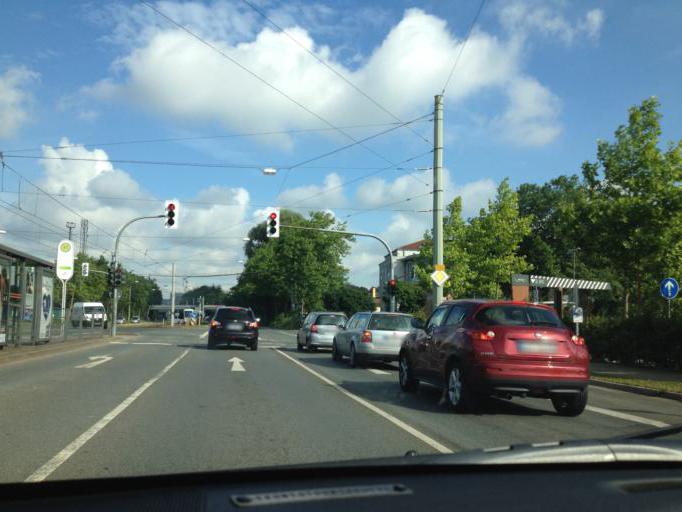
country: DE
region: North Rhine-Westphalia
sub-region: Regierungsbezirk Arnsberg
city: Bochum
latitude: 51.4682
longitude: 7.2702
